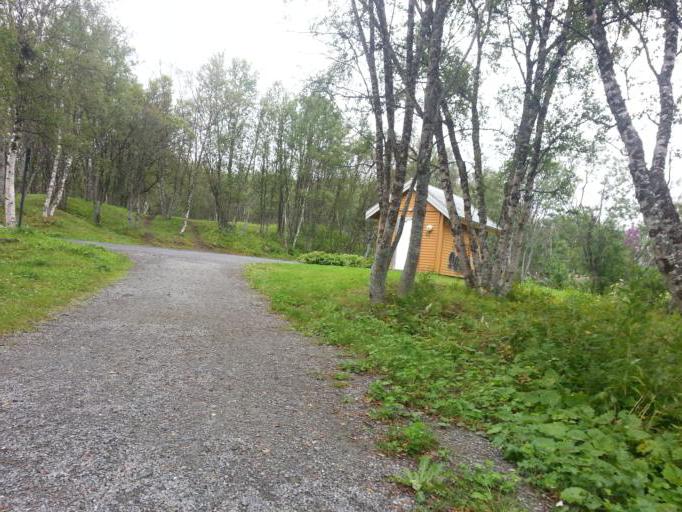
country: NO
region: Troms
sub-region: Tromso
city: Tromso
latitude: 69.6321
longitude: 18.9086
